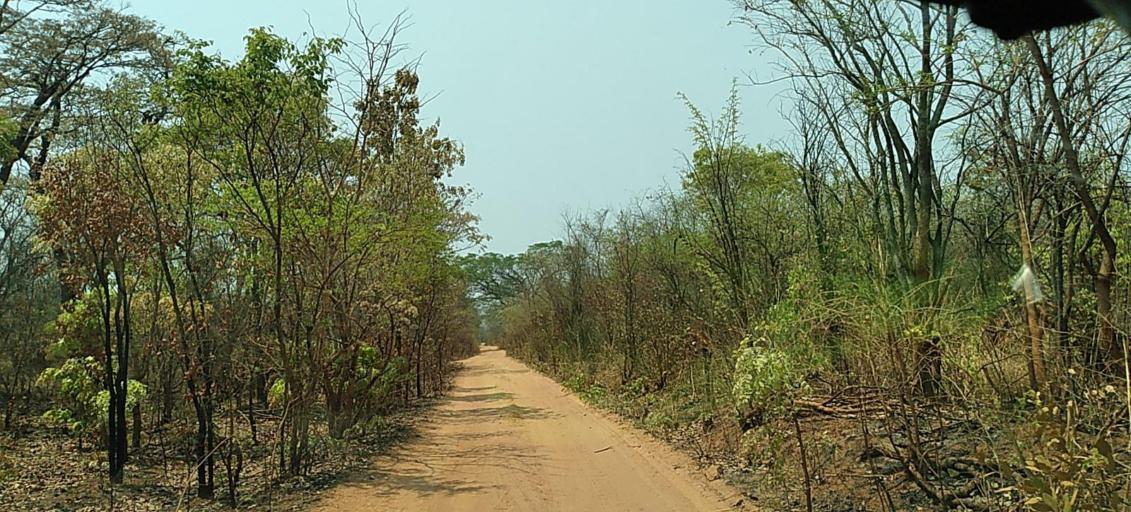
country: ZM
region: North-Western
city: Kabompo
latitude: -13.6993
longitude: 24.3159
